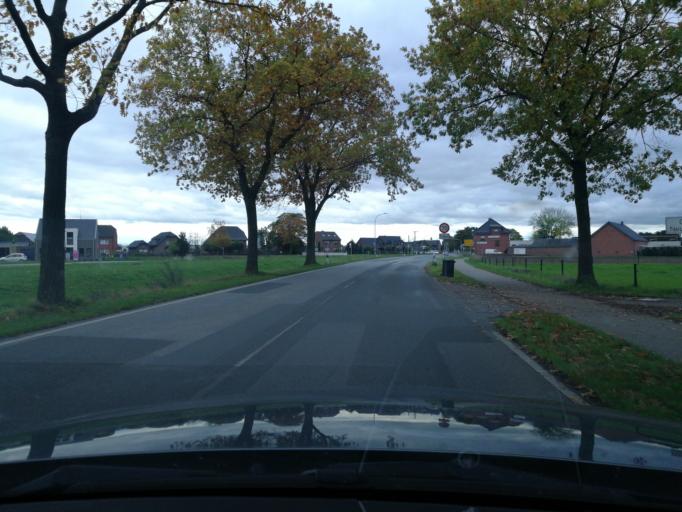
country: DE
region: North Rhine-Westphalia
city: Straelen
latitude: 51.4638
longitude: 6.2419
